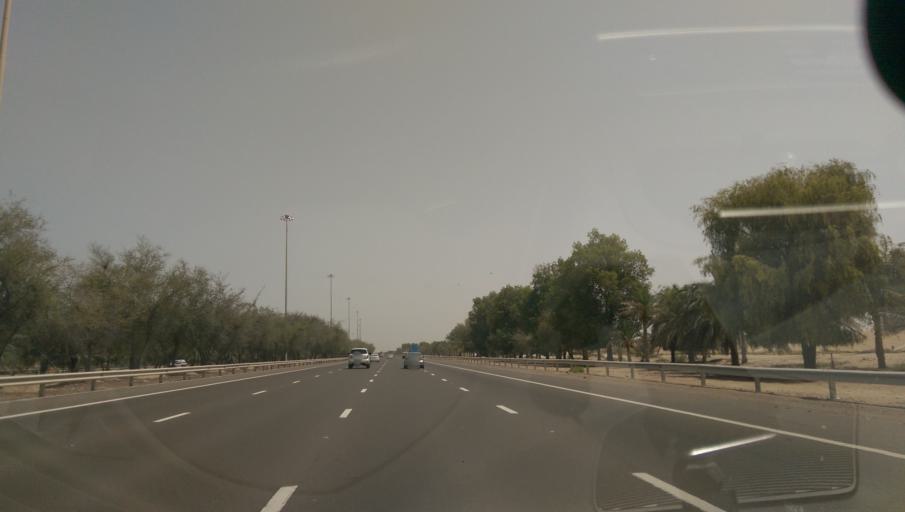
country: AE
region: Abu Dhabi
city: Abu Dhabi
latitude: 24.4449
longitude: 54.6788
